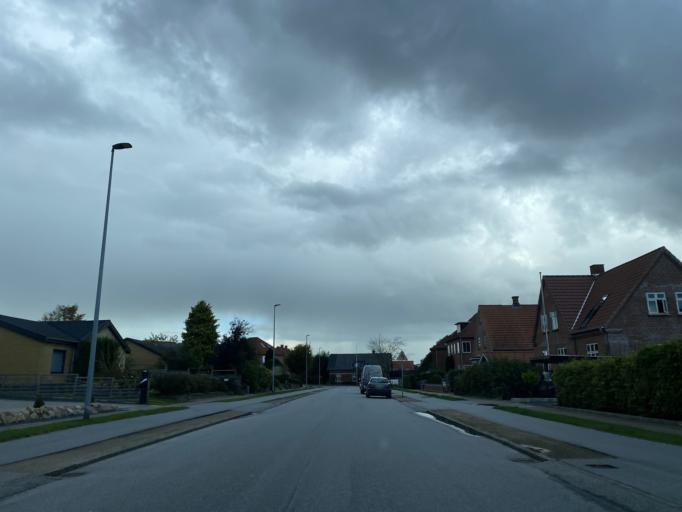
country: DK
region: South Denmark
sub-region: Haderslev Kommune
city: Haderslev
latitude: 55.2443
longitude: 9.4993
